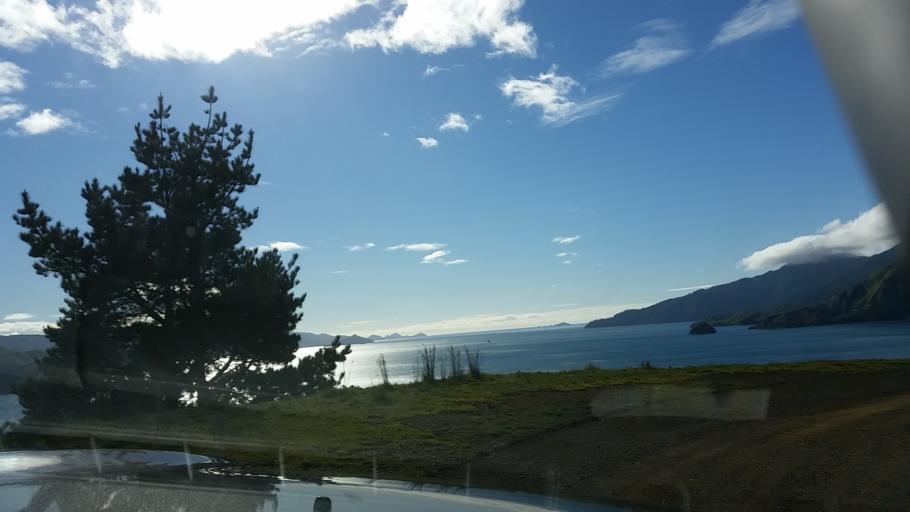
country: NZ
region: Marlborough
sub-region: Marlborough District
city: Picton
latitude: -40.9854
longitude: 173.8410
